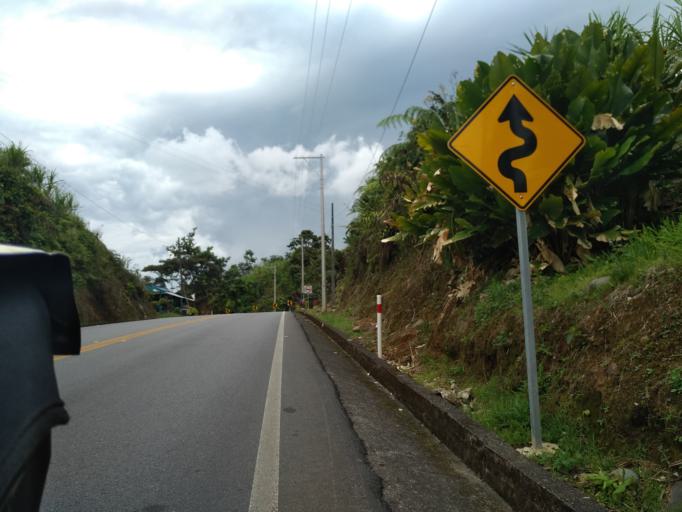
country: EC
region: Pastaza
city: Puyo
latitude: -1.3376
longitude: -77.9116
